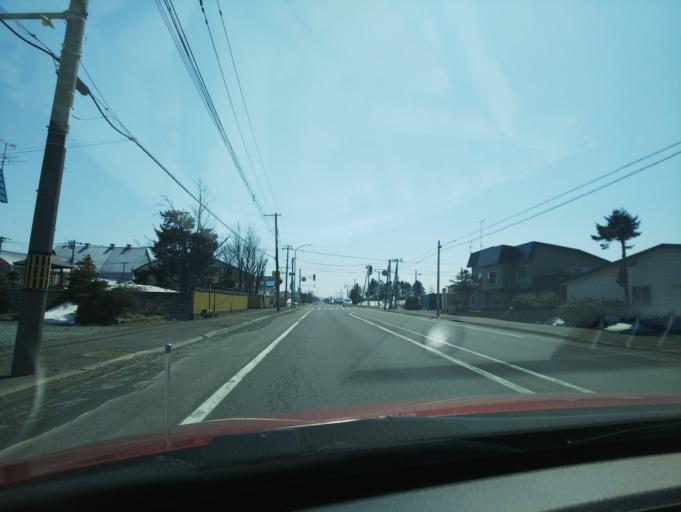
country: JP
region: Hokkaido
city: Nayoro
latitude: 44.2366
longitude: 142.3948
